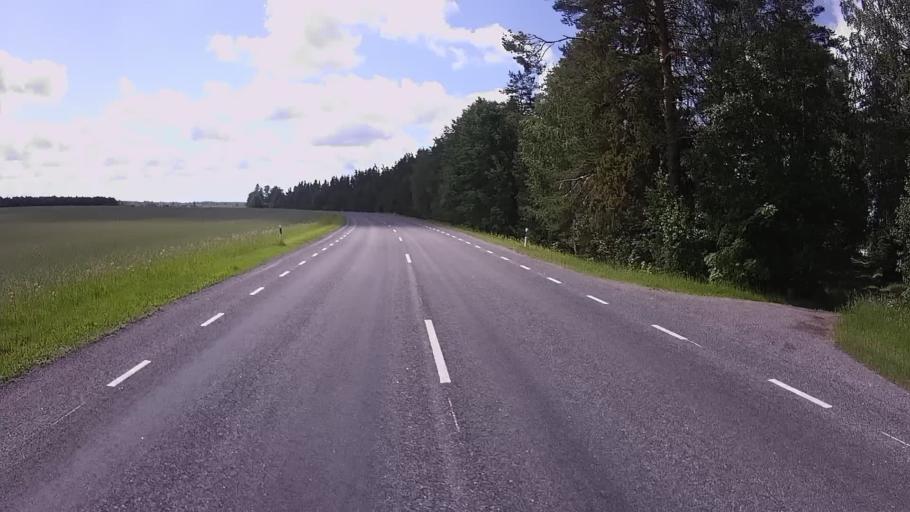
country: EE
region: Valgamaa
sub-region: Torva linn
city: Torva
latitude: 58.1193
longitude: 26.1324
